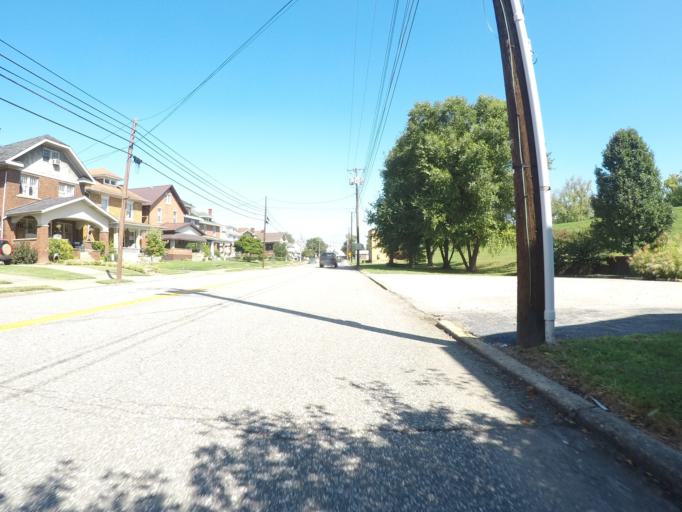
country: US
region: Kentucky
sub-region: Boyd County
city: Catlettsburg
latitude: 38.4108
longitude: -82.5982
